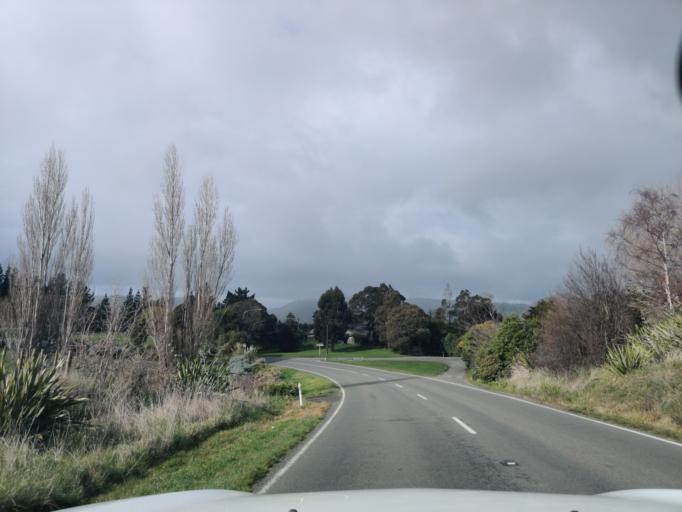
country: NZ
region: Manawatu-Wanganui
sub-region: Palmerston North City
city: Palmerston North
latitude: -40.2961
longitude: 175.7437
